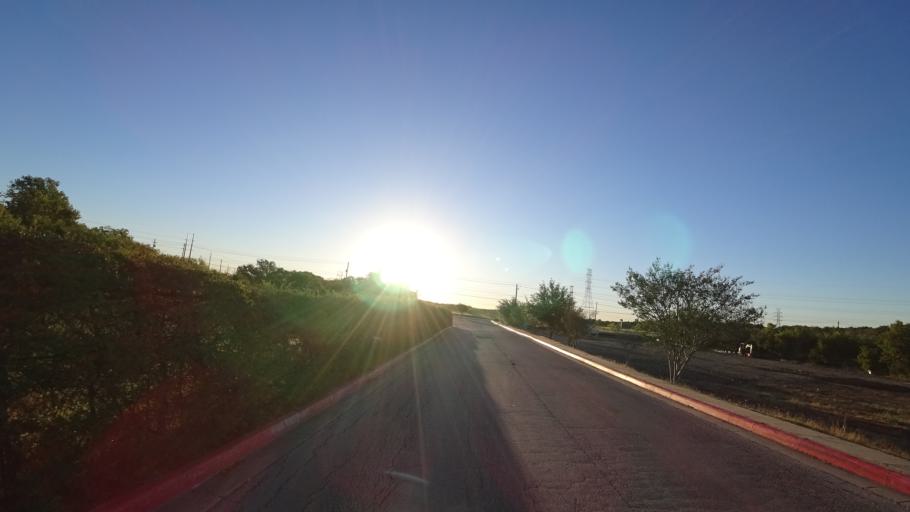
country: US
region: Texas
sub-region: Travis County
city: Hornsby Bend
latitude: 30.3056
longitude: -97.6201
